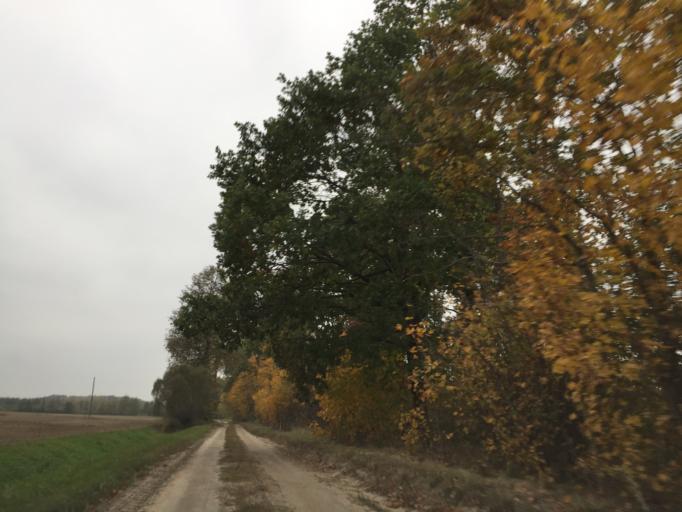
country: LV
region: Dobeles Rajons
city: Dobele
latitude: 56.6715
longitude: 23.4711
